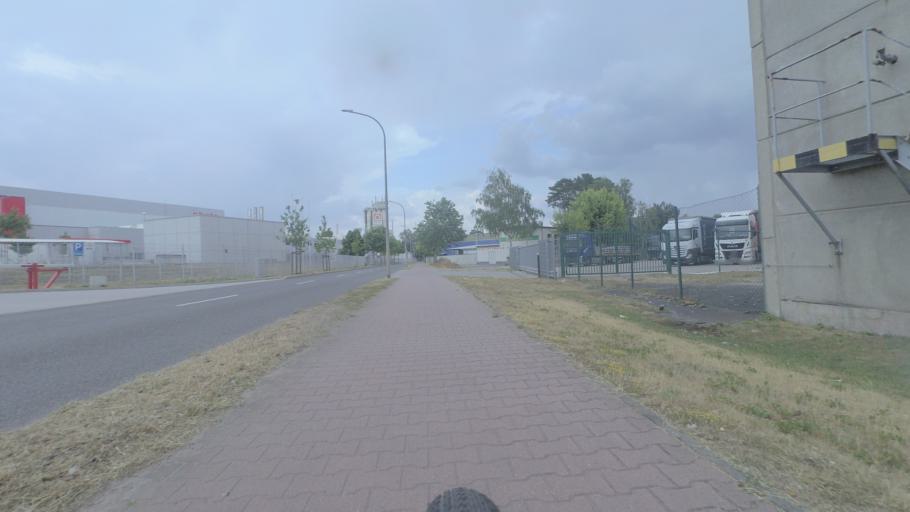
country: DE
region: Brandenburg
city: Ludwigsfelde
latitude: 52.3254
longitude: 13.2597
